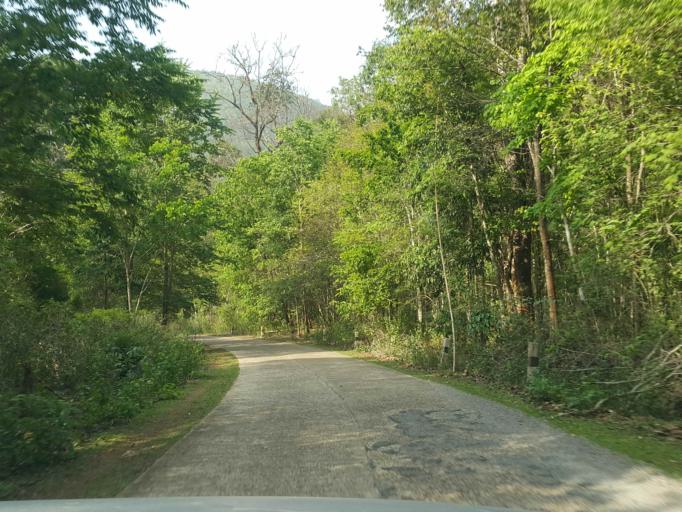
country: TH
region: Chiang Mai
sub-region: Amphoe Chiang Dao
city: Chiang Dao
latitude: 19.3960
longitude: 98.7742
